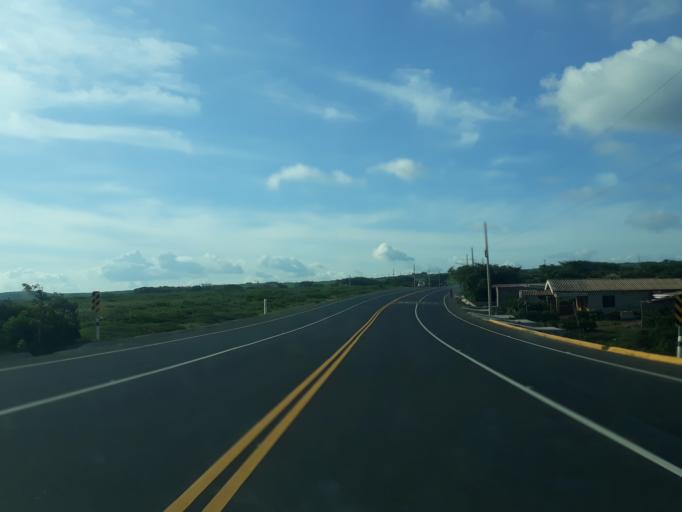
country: NI
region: Managua
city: El Crucero
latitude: 11.9459
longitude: -86.2994
